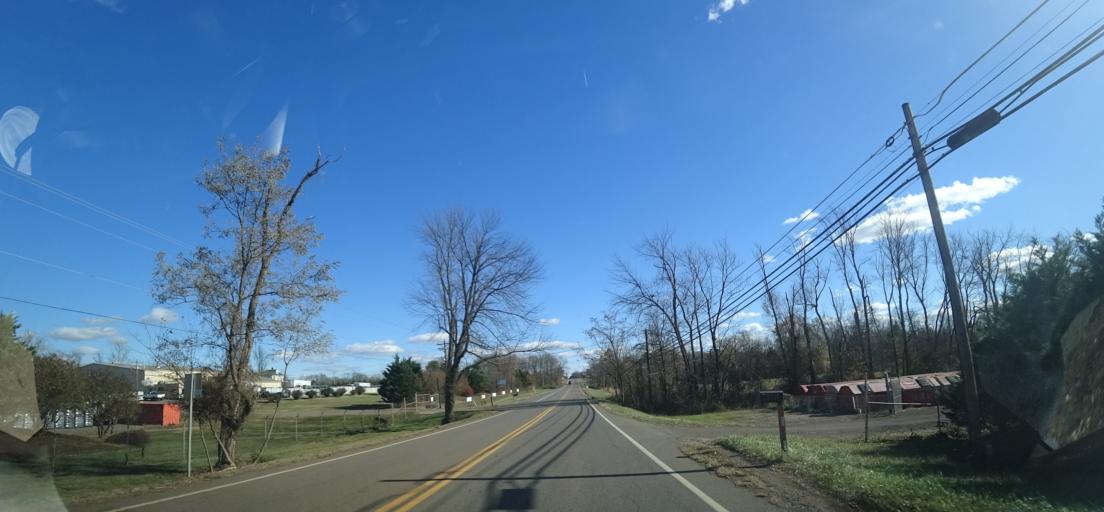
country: US
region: Virginia
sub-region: Culpeper County
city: Culpeper
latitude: 38.4868
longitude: -77.9507
